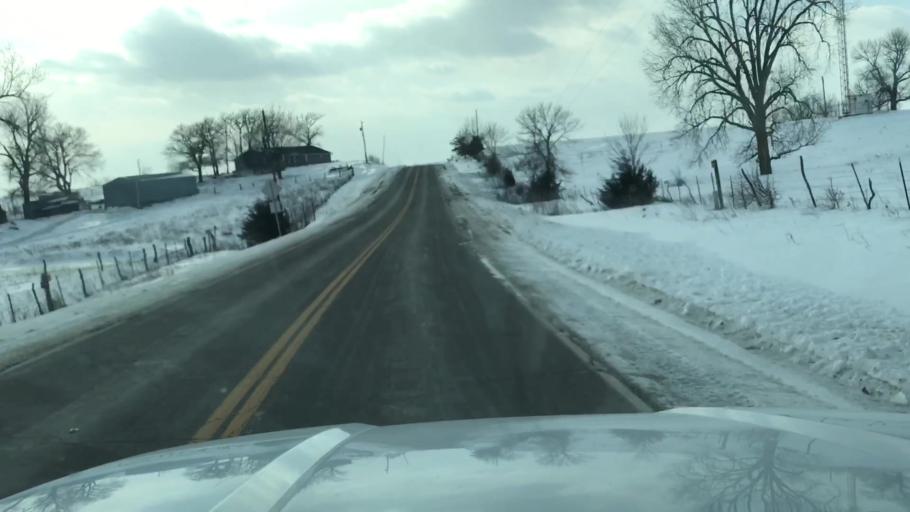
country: US
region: Missouri
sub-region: Gentry County
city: Stanberry
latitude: 40.3669
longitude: -94.6492
